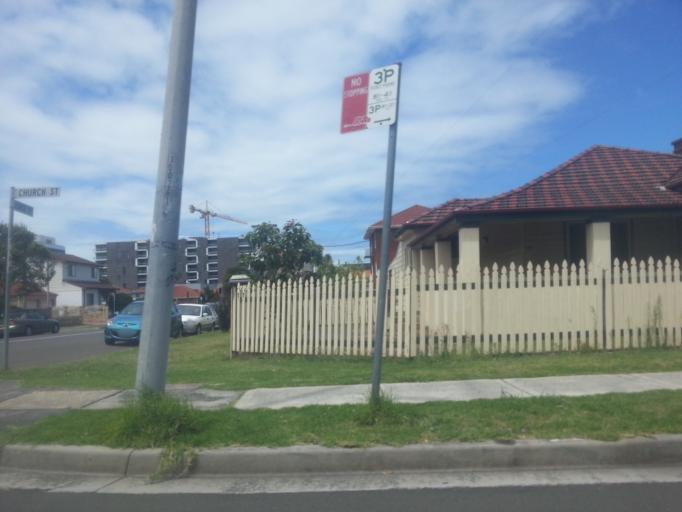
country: AU
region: New South Wales
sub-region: Wollongong
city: Wollongong
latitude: -34.4283
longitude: 150.8947
